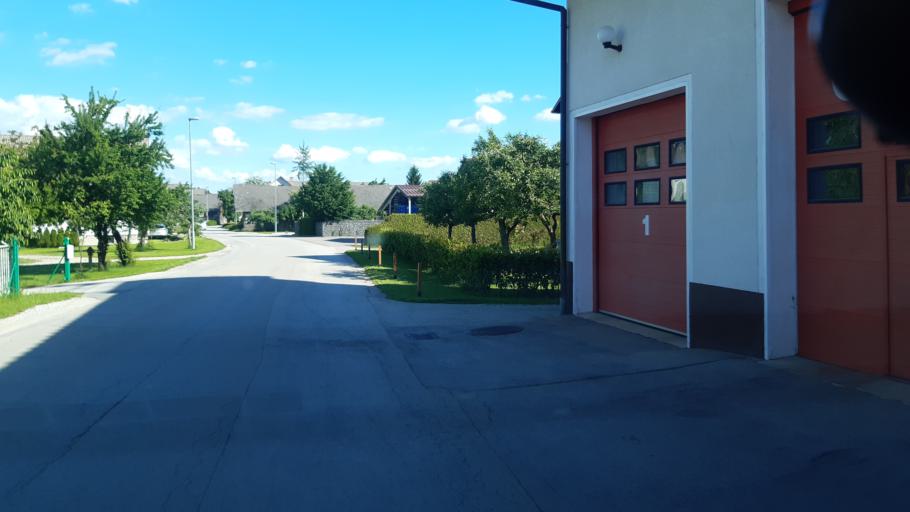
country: SI
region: Sencur
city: Hrastje
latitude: 46.2126
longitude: 14.3856
